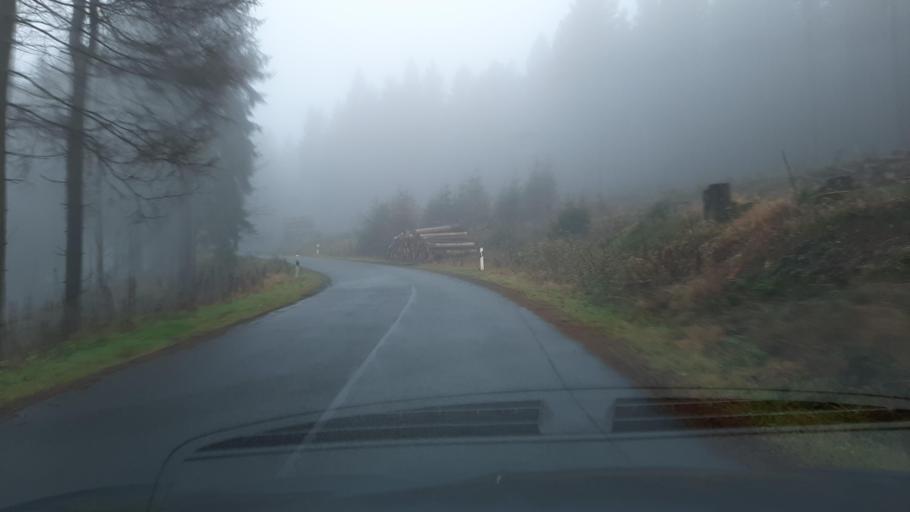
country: DE
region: North Rhine-Westphalia
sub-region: Regierungsbezirk Arnsberg
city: Winterberg
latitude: 51.1755
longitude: 8.4952
